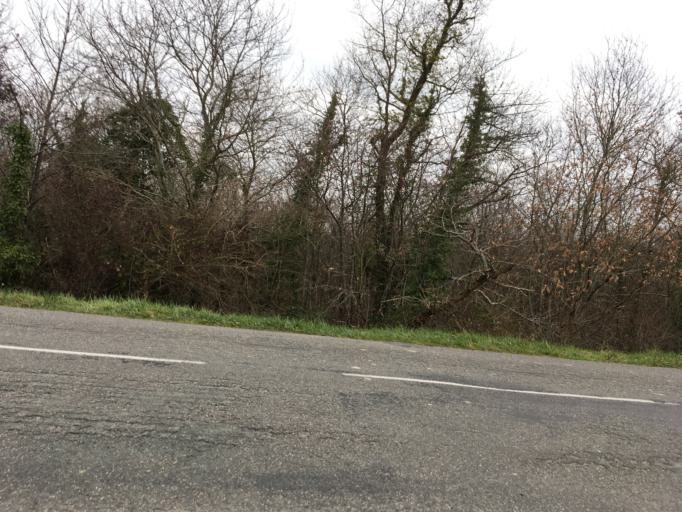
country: FR
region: Aquitaine
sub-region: Departement de la Gironde
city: Saint-Ciers-sur-Gironde
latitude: 45.3183
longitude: -0.5947
